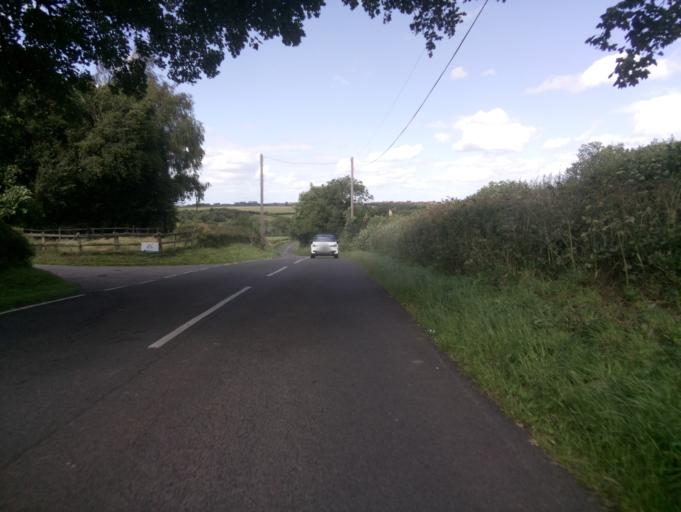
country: GB
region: England
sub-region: Nottinghamshire
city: East Leake
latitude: 52.8202
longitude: -1.2097
